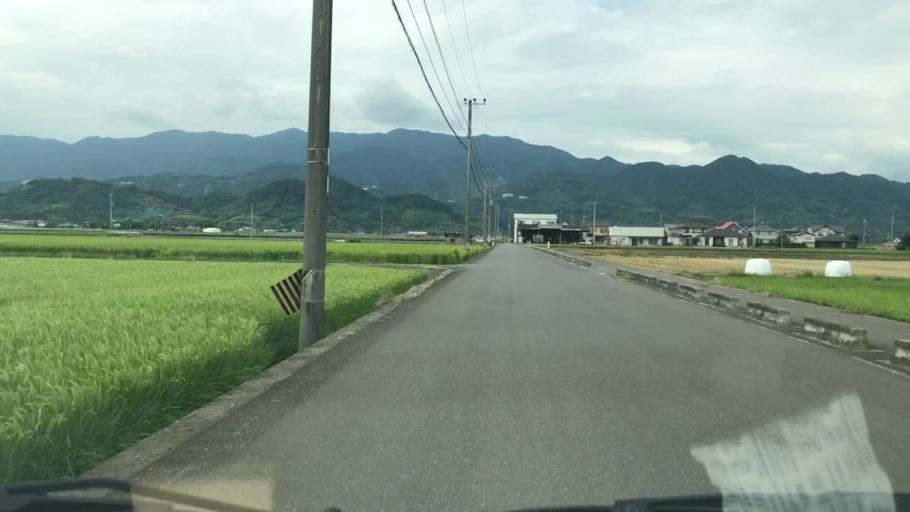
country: JP
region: Saga Prefecture
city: Saga-shi
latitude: 33.2868
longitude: 130.2251
